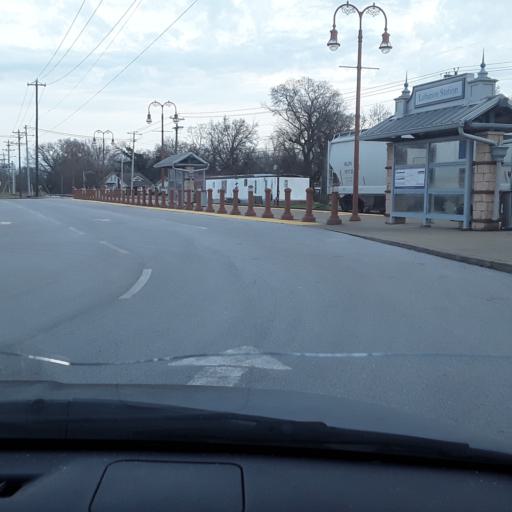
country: US
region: Tennessee
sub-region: Wilson County
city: Lebanon
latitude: 36.2124
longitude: -86.2976
